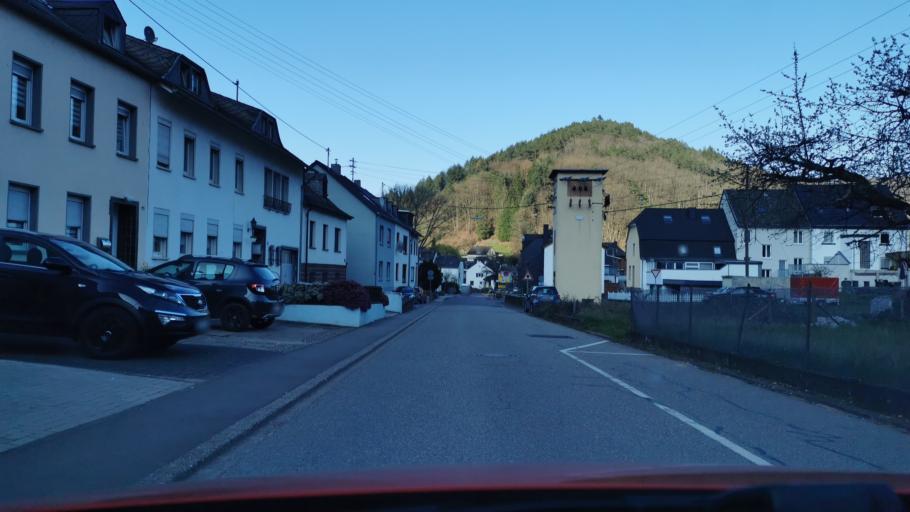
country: DE
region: Rheinland-Pfalz
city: Kordel
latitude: 49.8364
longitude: 6.6318
